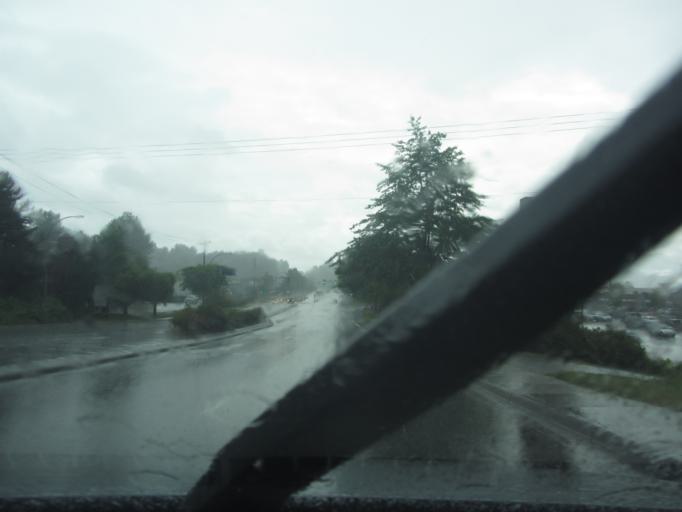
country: CA
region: British Columbia
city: Abbotsford
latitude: 49.1329
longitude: -122.3246
